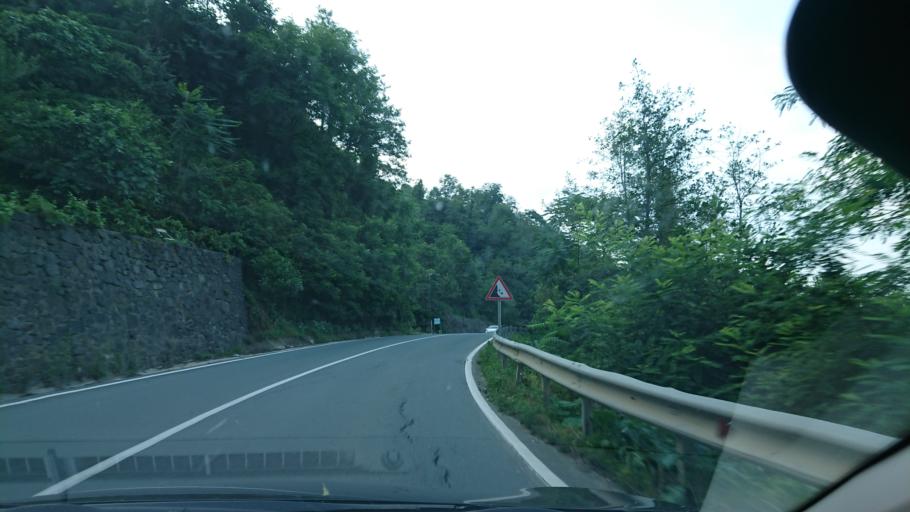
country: TR
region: Rize
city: Cayeli
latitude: 41.0722
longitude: 40.7112
